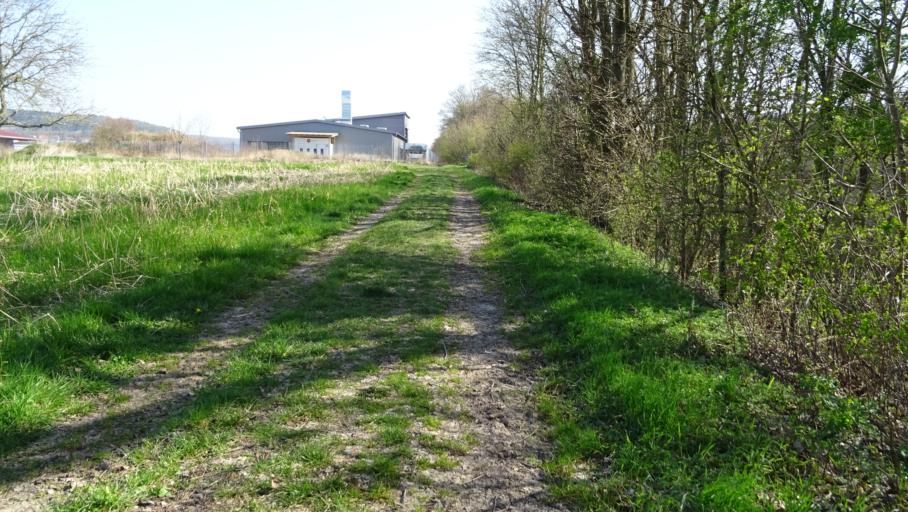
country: DE
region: Baden-Wuerttemberg
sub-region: Karlsruhe Region
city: Obrigheim
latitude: 49.3351
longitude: 9.1089
